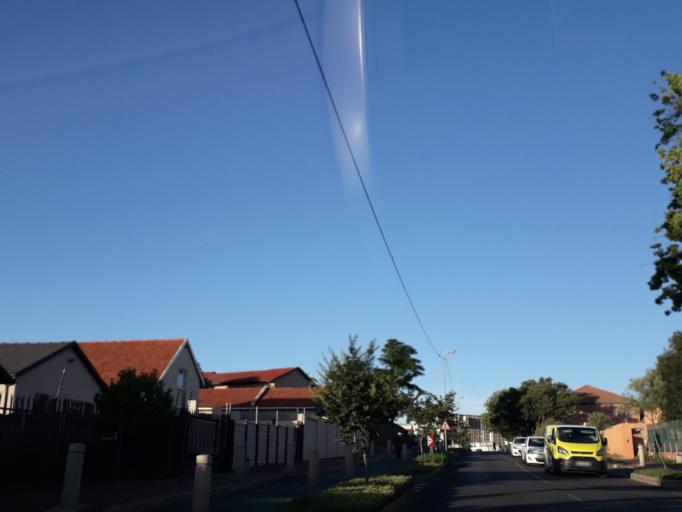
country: ZA
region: Gauteng
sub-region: City of Johannesburg Metropolitan Municipality
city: Johannesburg
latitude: -26.1759
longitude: 27.9784
